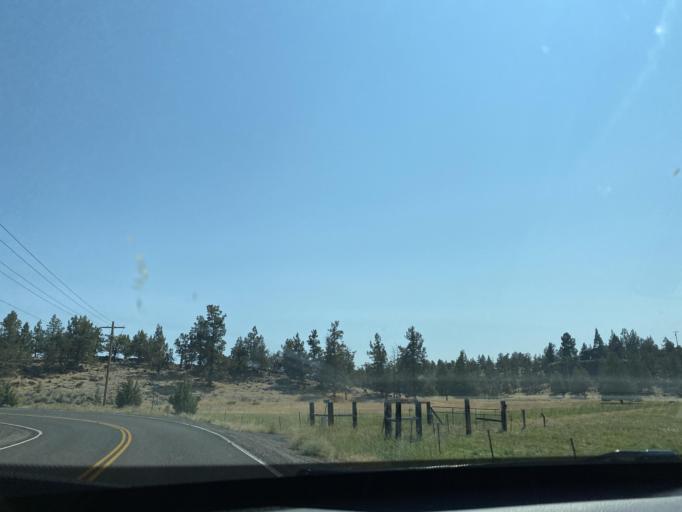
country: US
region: Oregon
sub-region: Deschutes County
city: Terrebonne
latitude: 44.3681
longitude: -121.1636
